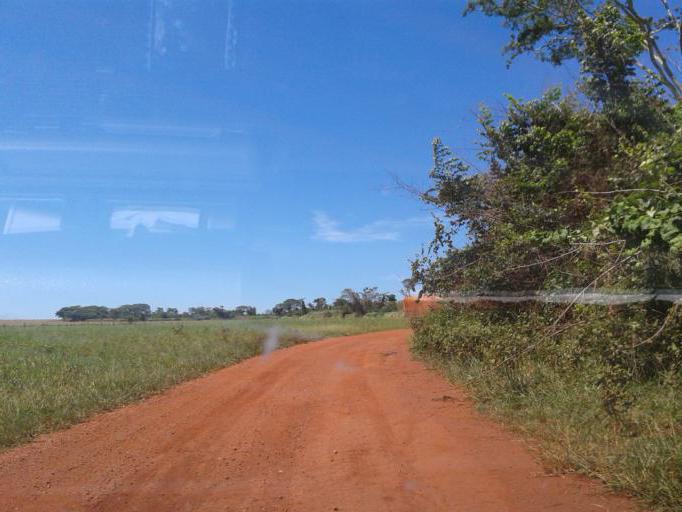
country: BR
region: Minas Gerais
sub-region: Capinopolis
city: Capinopolis
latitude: -18.6425
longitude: -49.6083
